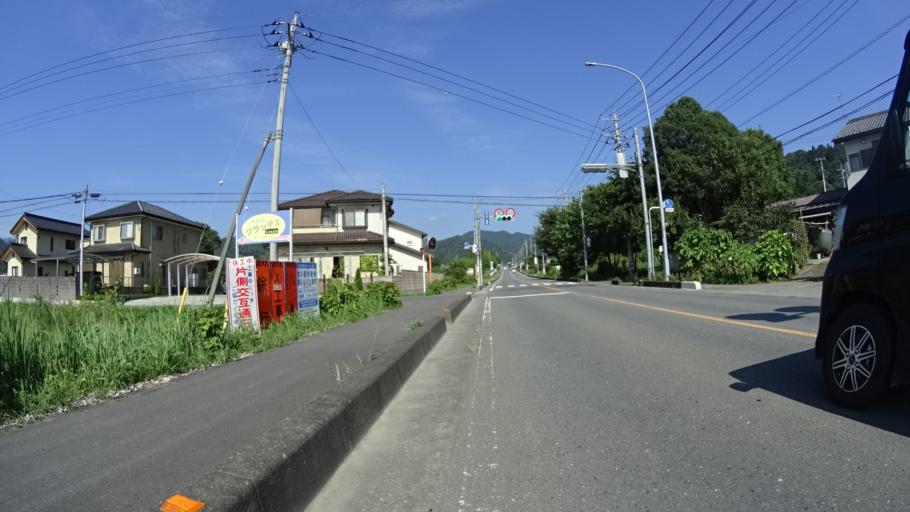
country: JP
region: Saitama
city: Chichibu
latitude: 36.0265
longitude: 138.9959
